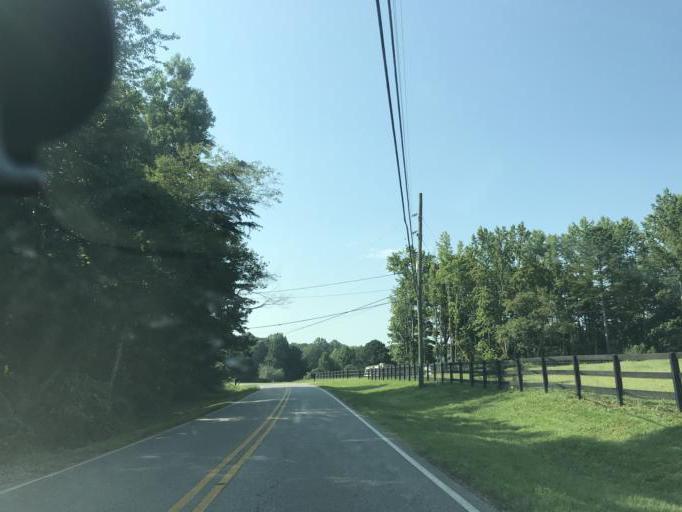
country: US
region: Georgia
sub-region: Forsyth County
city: Cumming
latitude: 34.2397
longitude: -84.1100
